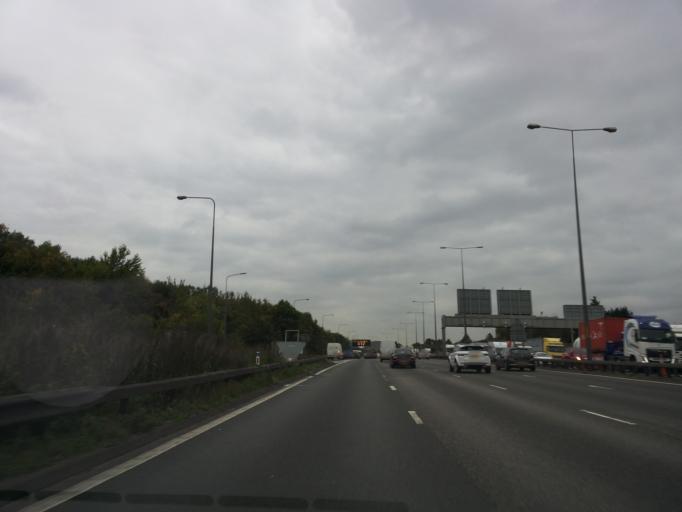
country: GB
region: England
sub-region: Kent
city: Dartford
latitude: 51.4517
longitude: 0.2405
